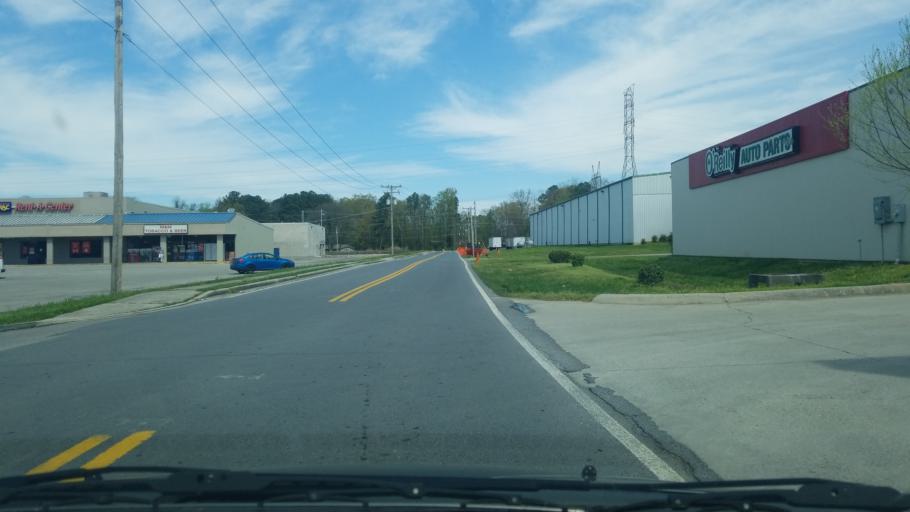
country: US
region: Georgia
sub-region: Catoosa County
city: Fort Oglethorpe
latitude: 34.9544
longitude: -85.2504
